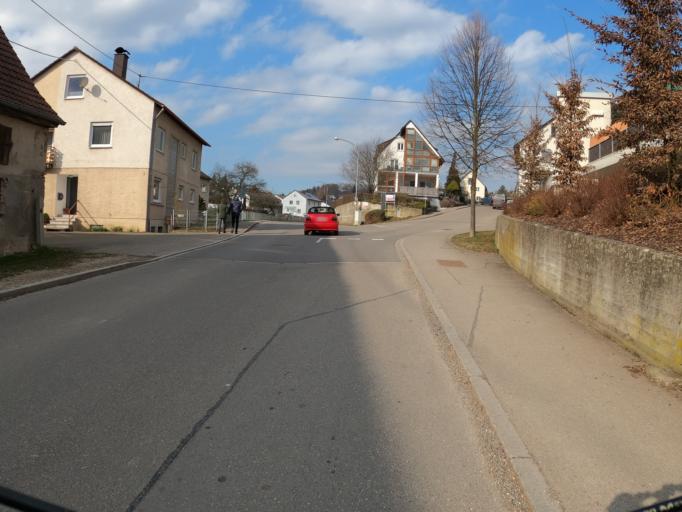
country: DE
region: Bavaria
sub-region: Swabia
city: Neu-Ulm
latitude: 48.4390
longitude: 10.0507
